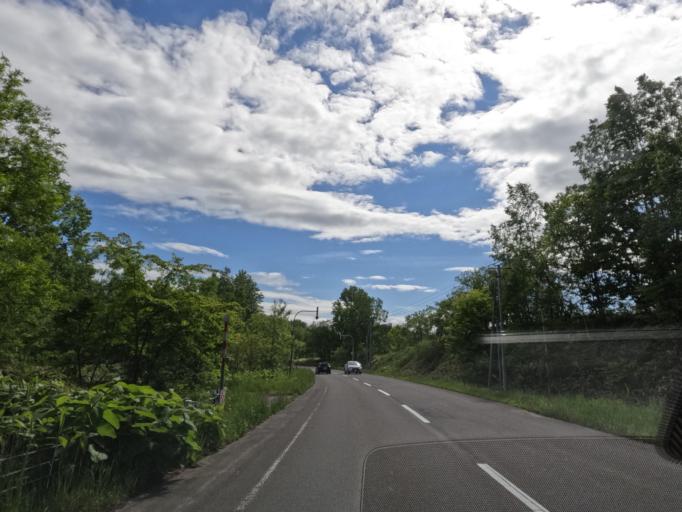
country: JP
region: Hokkaido
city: Kamikawa
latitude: 43.8776
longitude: 142.5733
